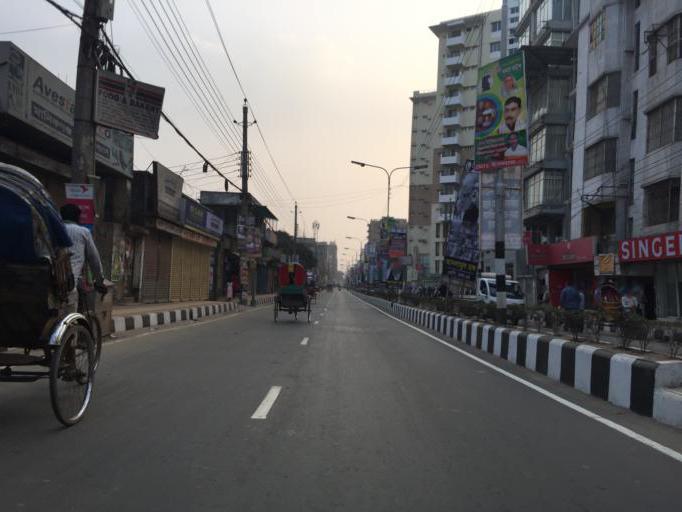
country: BD
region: Dhaka
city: Azimpur
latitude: 23.7914
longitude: 90.3485
